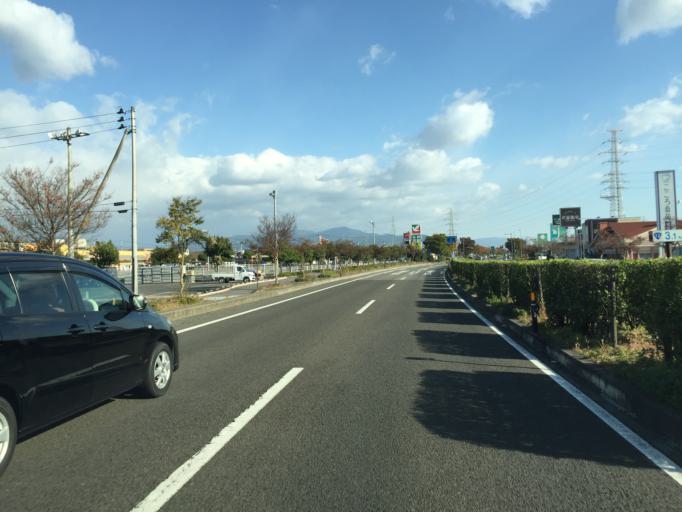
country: JP
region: Fukushima
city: Fukushima-shi
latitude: 37.7677
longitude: 140.4370
